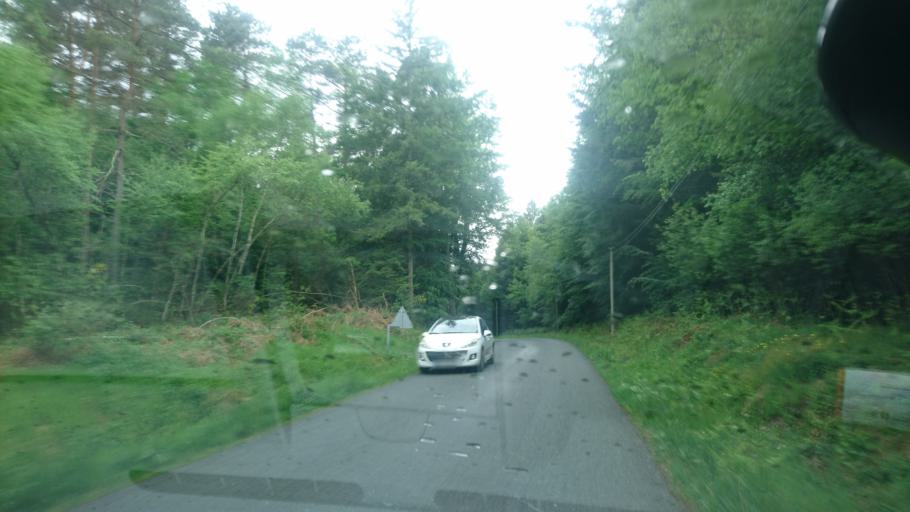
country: FR
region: Limousin
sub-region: Departement de la Haute-Vienne
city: Peyrat-le-Chateau
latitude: 45.8313
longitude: 1.8505
